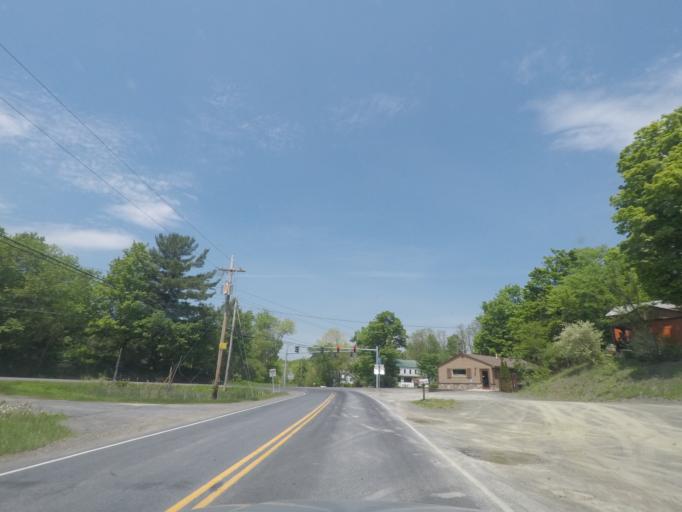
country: US
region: New York
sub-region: Rensselaer County
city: West Sand Lake
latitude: 42.6045
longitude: -73.6057
